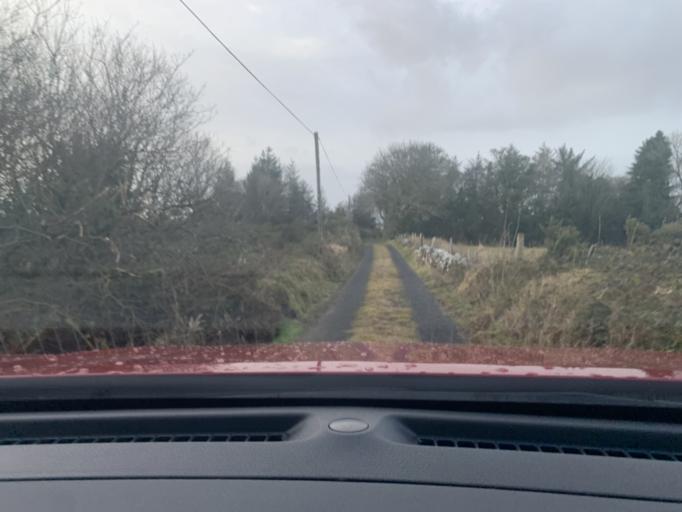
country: IE
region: Connaught
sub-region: Roscommon
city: Ballaghaderreen
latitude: 53.9536
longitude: -8.5391
